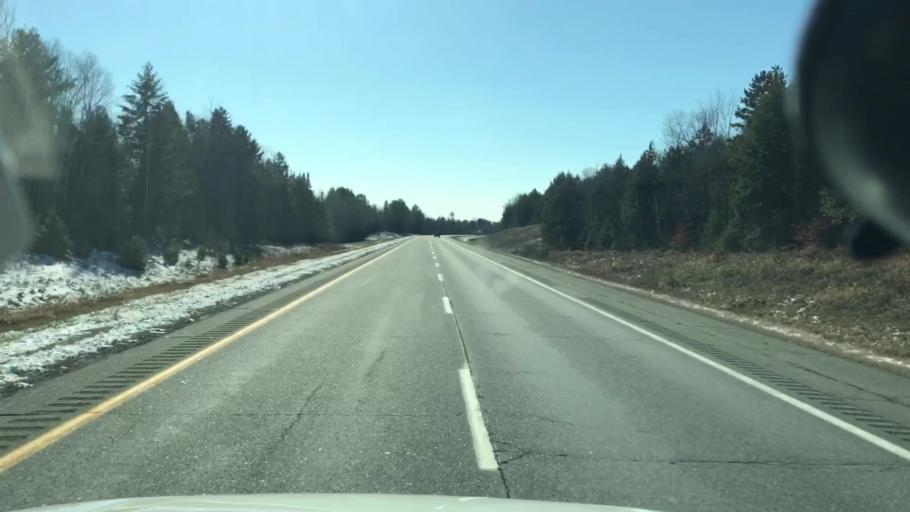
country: US
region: Maine
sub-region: Penobscot County
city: Howland
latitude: 45.2936
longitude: -68.6648
